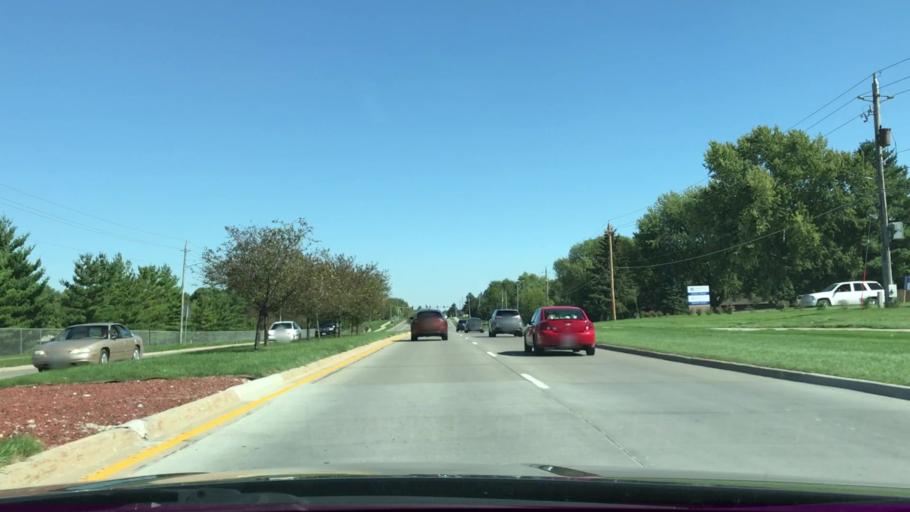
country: US
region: Iowa
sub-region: Polk County
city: Altoona
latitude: 41.6441
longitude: -93.4964
